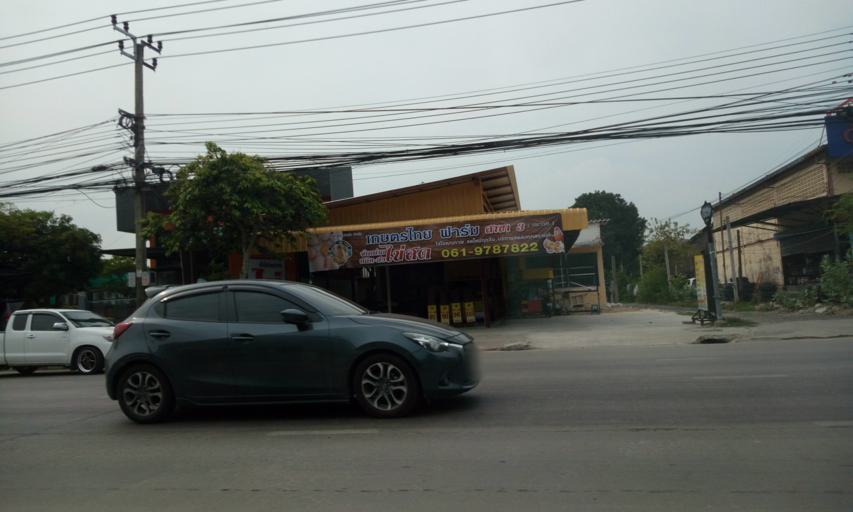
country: TH
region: Bangkok
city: Saphan Sung
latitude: 13.7221
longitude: 100.7144
